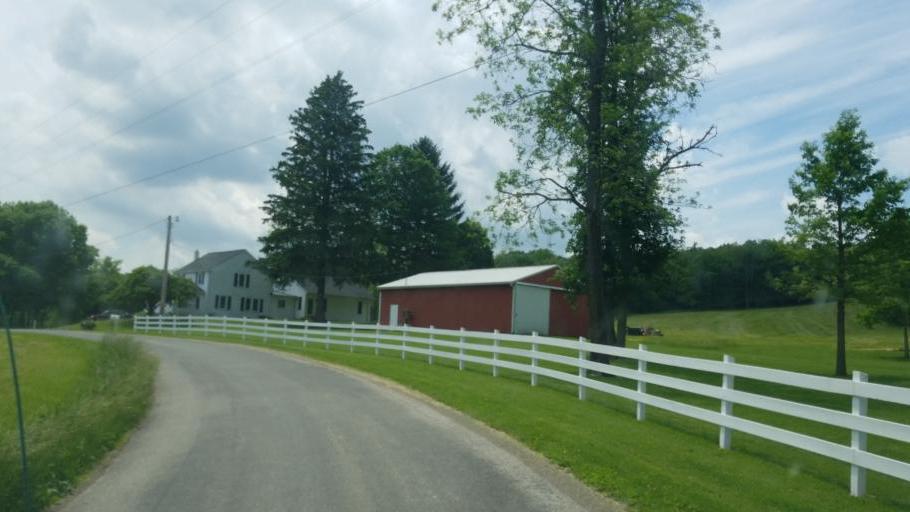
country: US
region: Ohio
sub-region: Ashland County
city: Ashland
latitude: 40.7691
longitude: -82.3406
